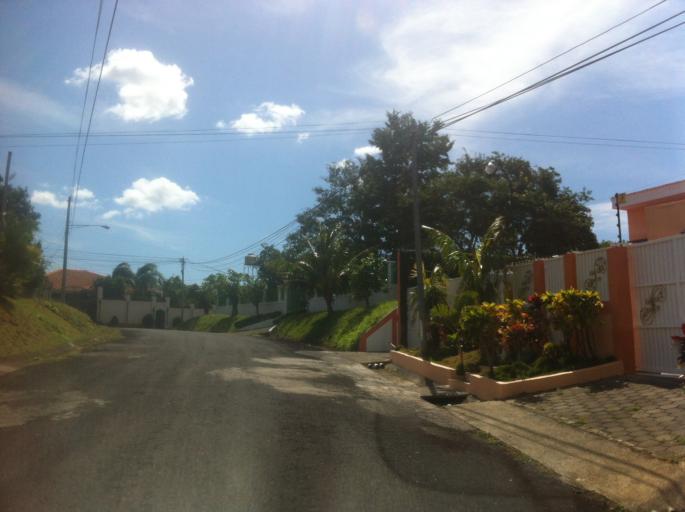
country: NI
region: Managua
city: El Crucero
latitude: 12.0742
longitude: -86.3224
